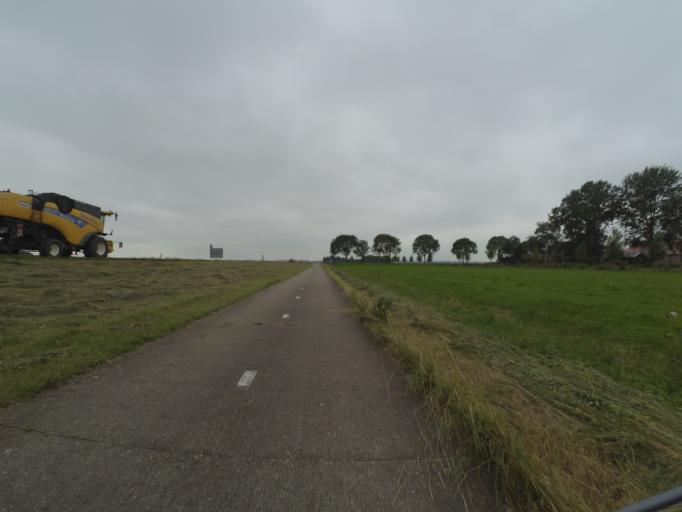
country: NL
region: Flevoland
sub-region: Gemeente Lelystad
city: Lelystad
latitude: 52.4441
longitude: 5.5505
